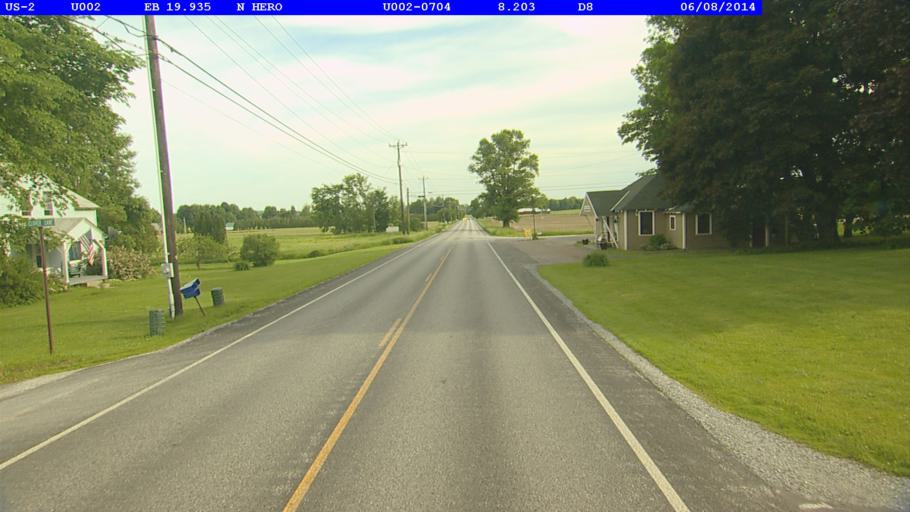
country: US
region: Vermont
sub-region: Grand Isle County
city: North Hero
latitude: 44.7816
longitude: -73.2935
